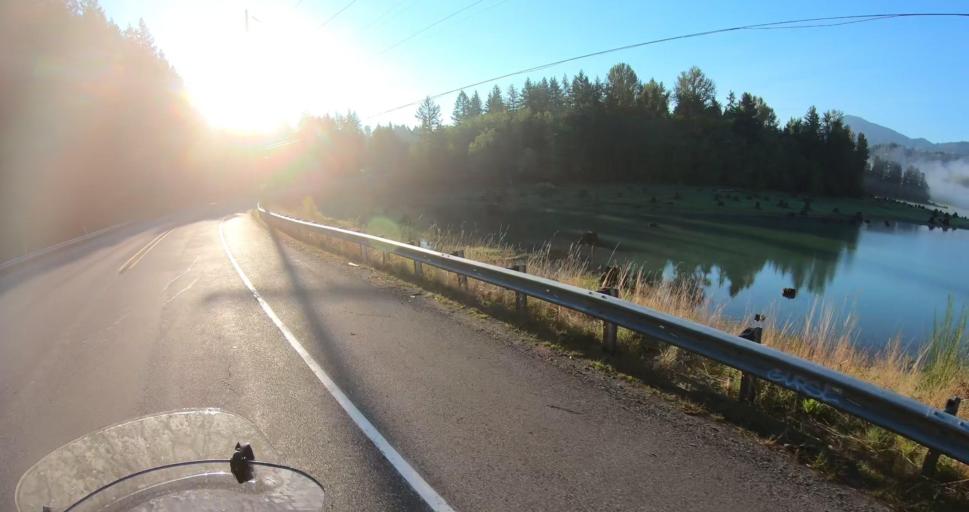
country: US
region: Washington
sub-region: Pierce County
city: Eatonville
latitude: 46.7956
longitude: -122.2772
